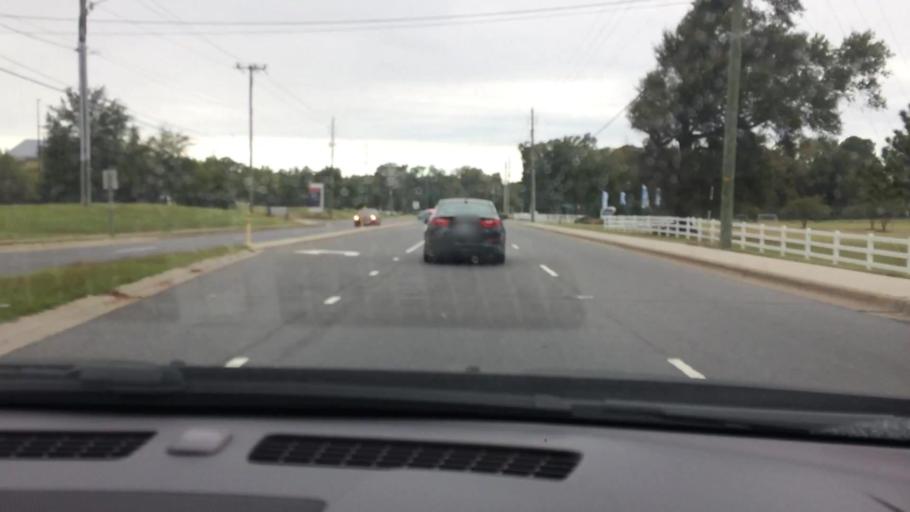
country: US
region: North Carolina
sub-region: Pitt County
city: Greenville
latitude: 35.6137
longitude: -77.4029
